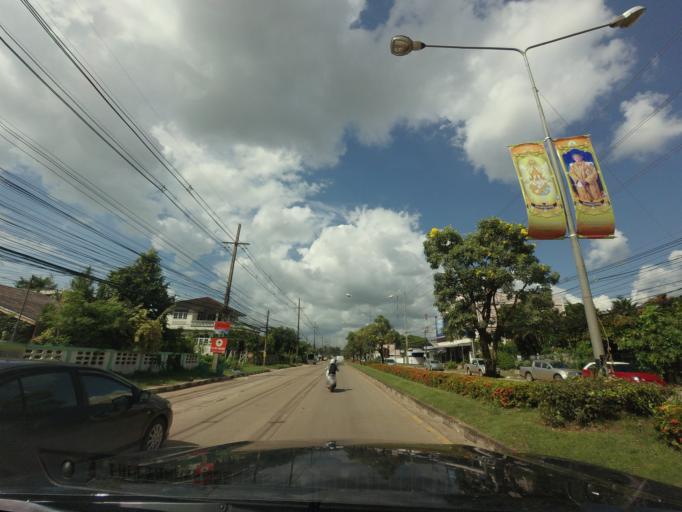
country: TH
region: Changwat Udon Thani
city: Udon Thani
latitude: 17.4303
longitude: 102.7773
